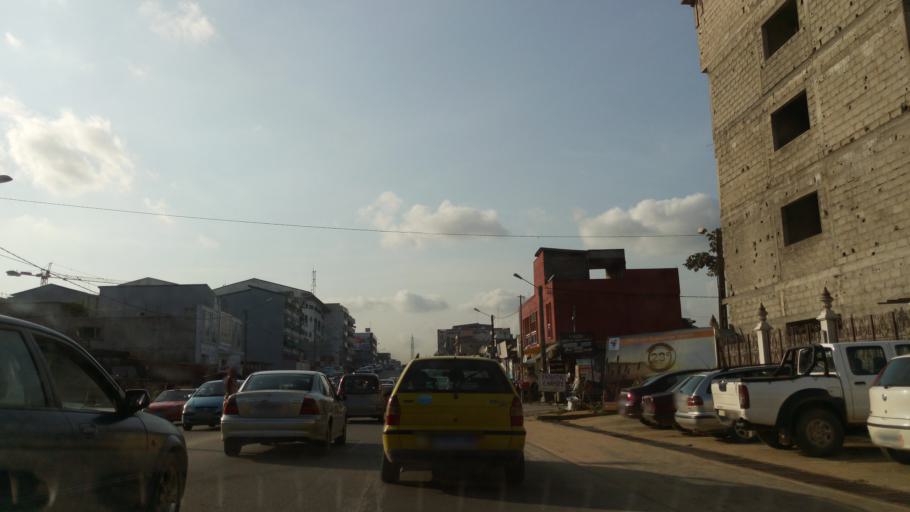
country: CI
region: Lagunes
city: Abobo
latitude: 5.3934
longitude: -3.9763
